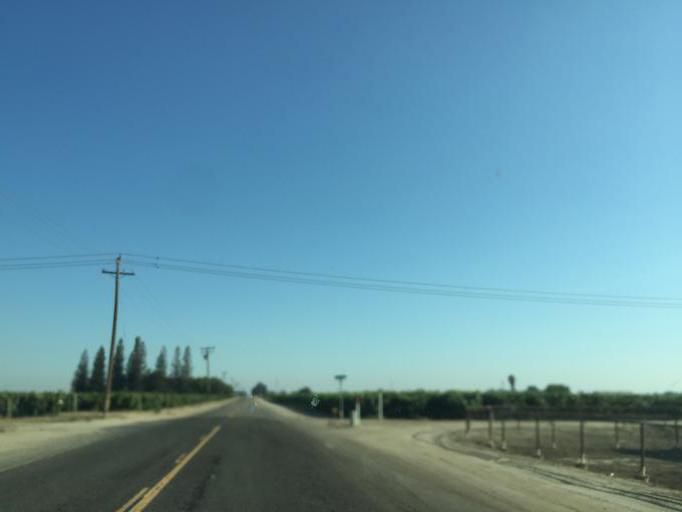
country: US
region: California
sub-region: Fresno County
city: Kingsburg
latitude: 36.4749
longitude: -119.5284
